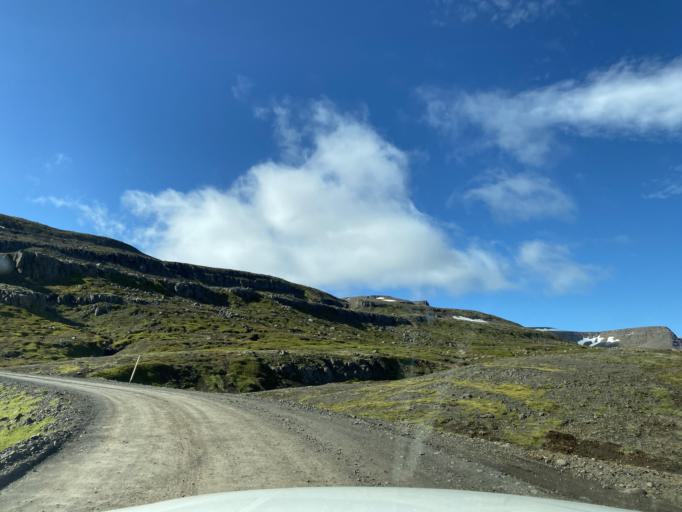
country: IS
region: East
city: Eskifjoerdur
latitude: 65.1786
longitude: -14.0998
